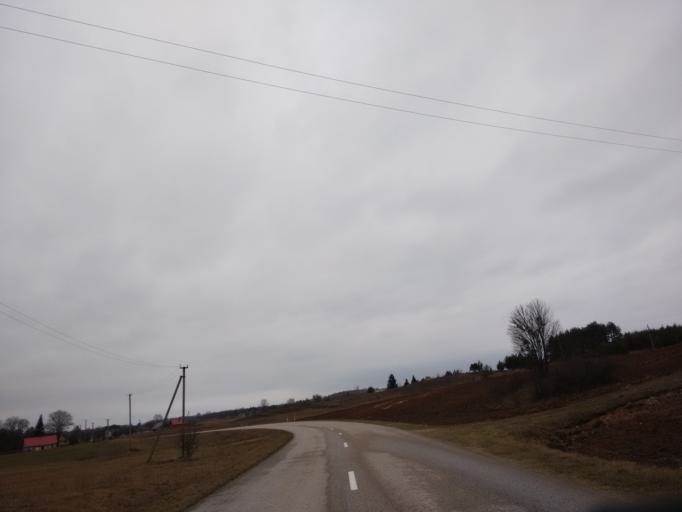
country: LT
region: Alytaus apskritis
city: Druskininkai
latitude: 54.2246
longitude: 23.8927
